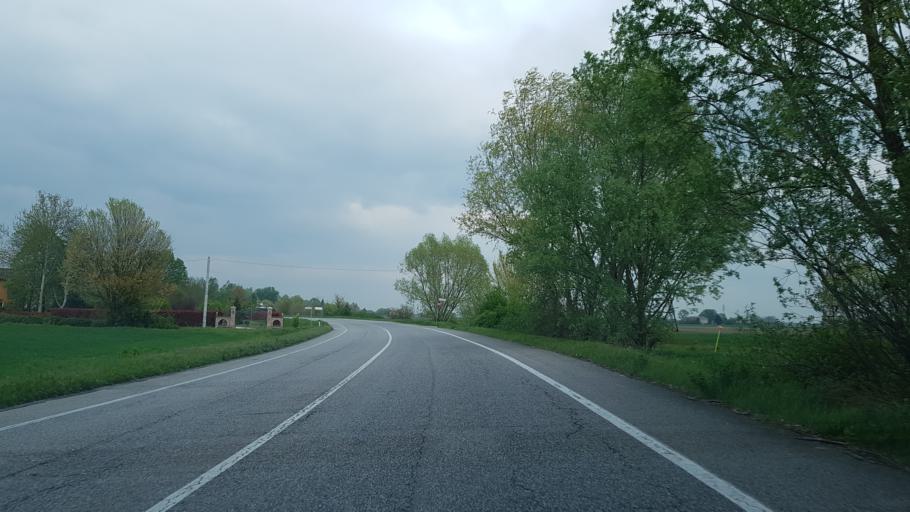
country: IT
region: Lombardy
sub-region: Provincia di Mantova
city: Ostiglia
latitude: 45.0851
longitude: 11.1437
